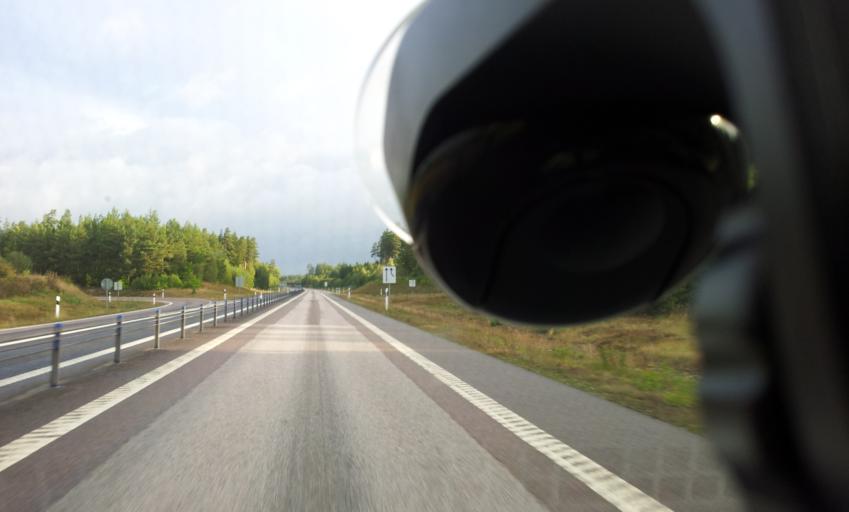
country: SE
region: Kalmar
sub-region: Torsas Kommun
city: Torsas
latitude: 56.5022
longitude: 16.0862
